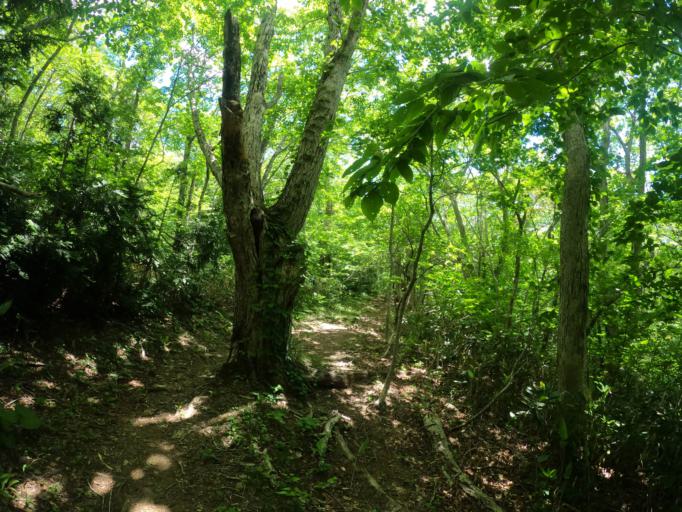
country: JP
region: Iwate
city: Ichinoseki
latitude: 38.9145
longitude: 140.8070
